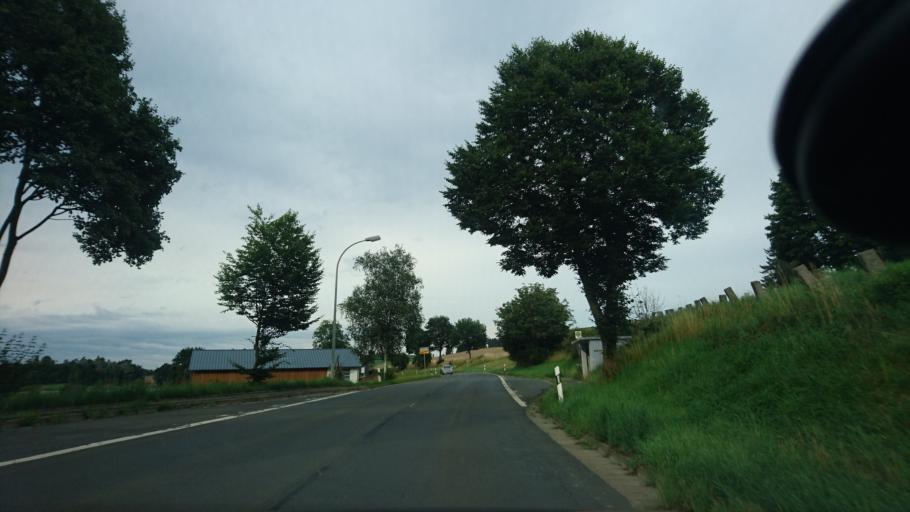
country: DE
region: Bavaria
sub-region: Upper Franconia
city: Selbitz
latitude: 50.3000
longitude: 11.7427
